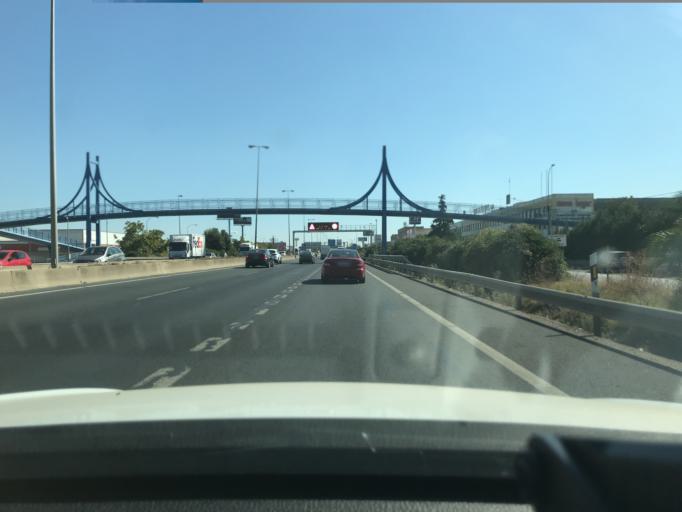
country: ES
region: Andalusia
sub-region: Provincia de Sevilla
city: Sevilla
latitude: 37.3939
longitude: -5.9438
